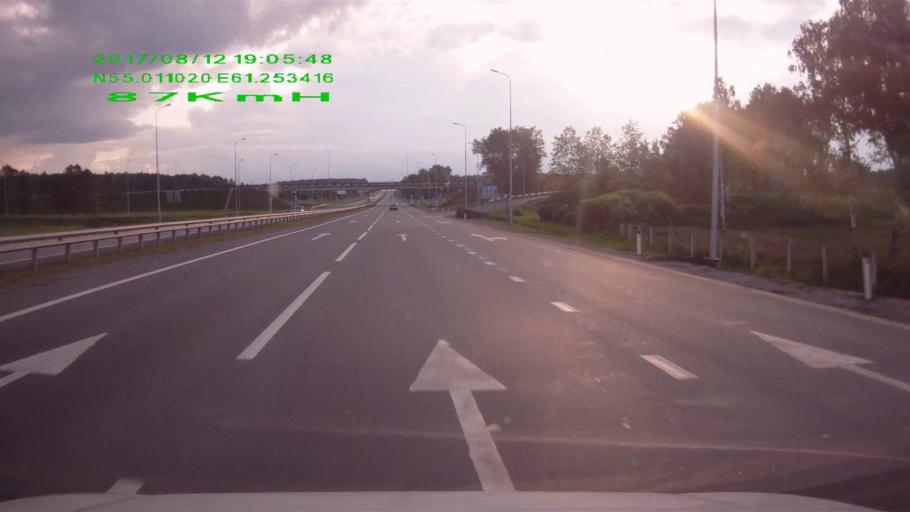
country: RU
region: Chelyabinsk
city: Sargazy
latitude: 55.0098
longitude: 61.2360
